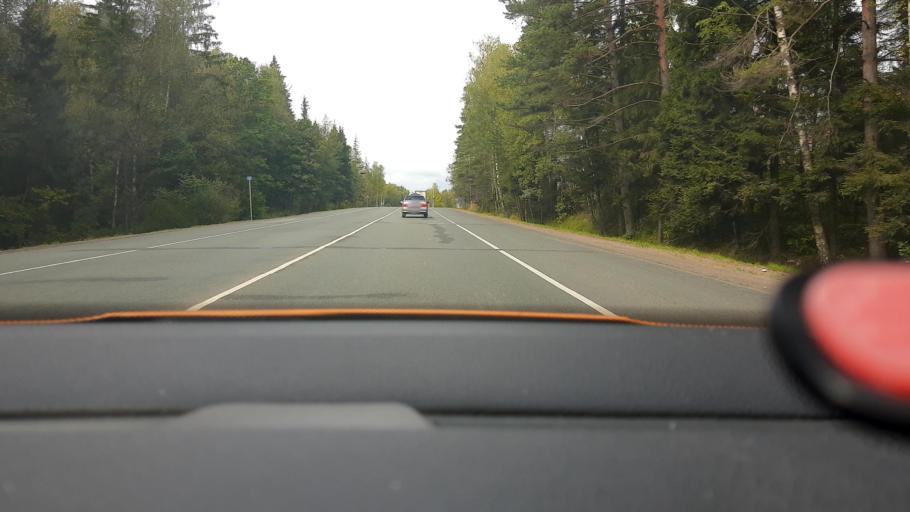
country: RU
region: Moskovskaya
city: Zelenogradskiy
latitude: 56.0858
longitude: 37.9980
